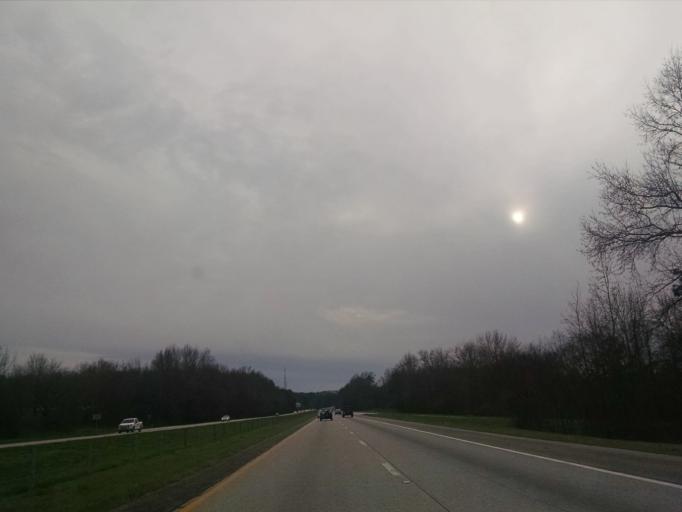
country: US
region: Georgia
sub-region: Hall County
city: Oakwood
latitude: 34.2097
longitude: -83.8867
